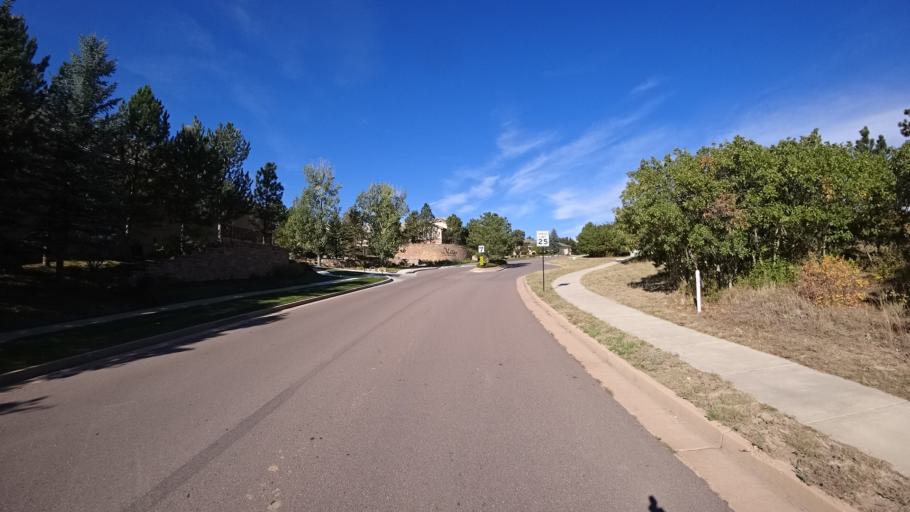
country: US
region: Colorado
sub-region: El Paso County
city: Colorado Springs
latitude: 38.9110
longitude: -104.7931
